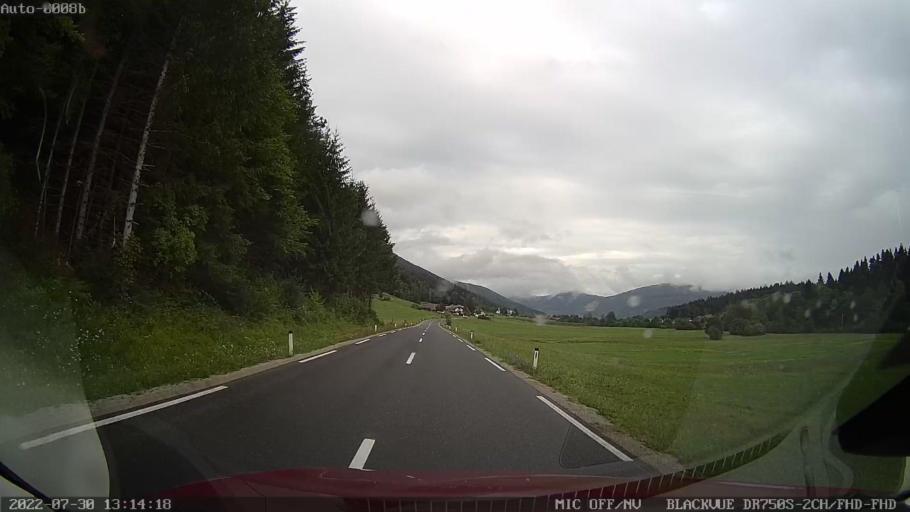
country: SI
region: Dolenjske Toplice
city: Dolenjske Toplice
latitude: 45.7292
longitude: 15.0494
